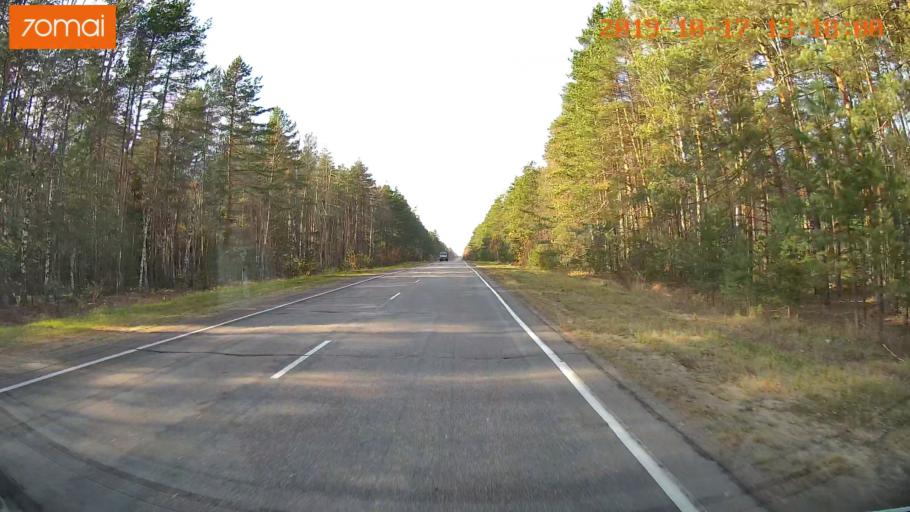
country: RU
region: Rjazan
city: Gus'-Zheleznyy
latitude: 55.0603
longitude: 41.1079
